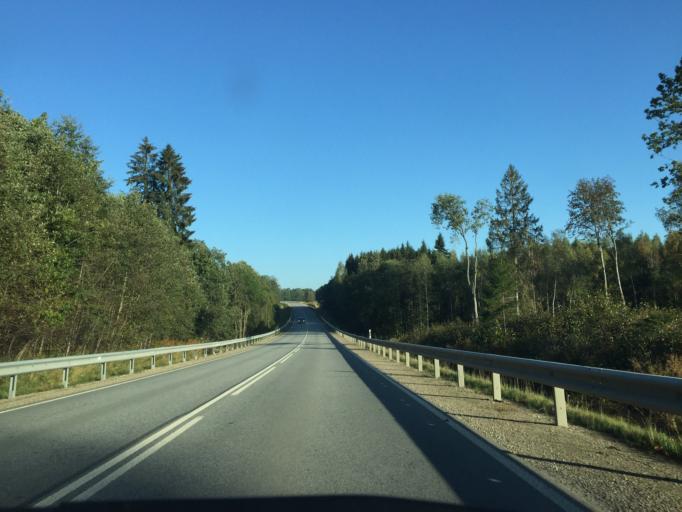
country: LV
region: Raunas
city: Rauna
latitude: 57.1810
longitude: 25.6206
